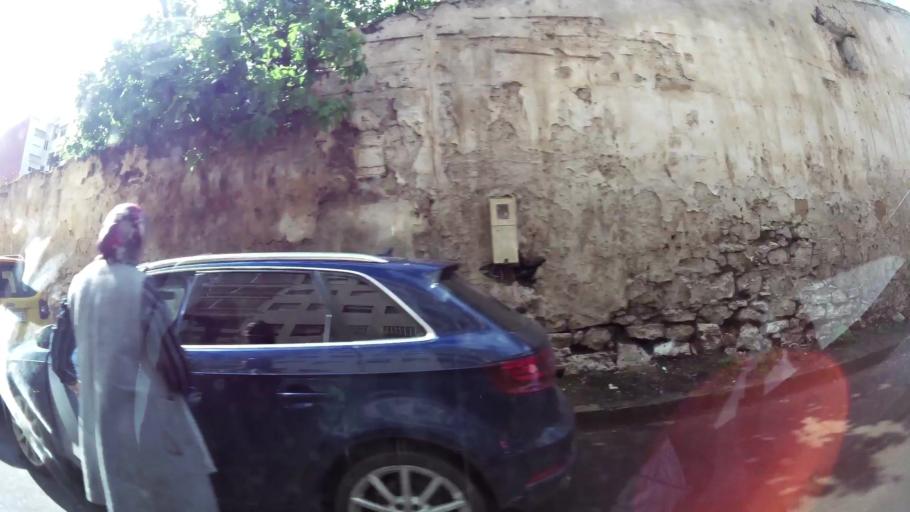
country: MA
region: Grand Casablanca
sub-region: Casablanca
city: Casablanca
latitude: 33.5707
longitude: -7.6268
